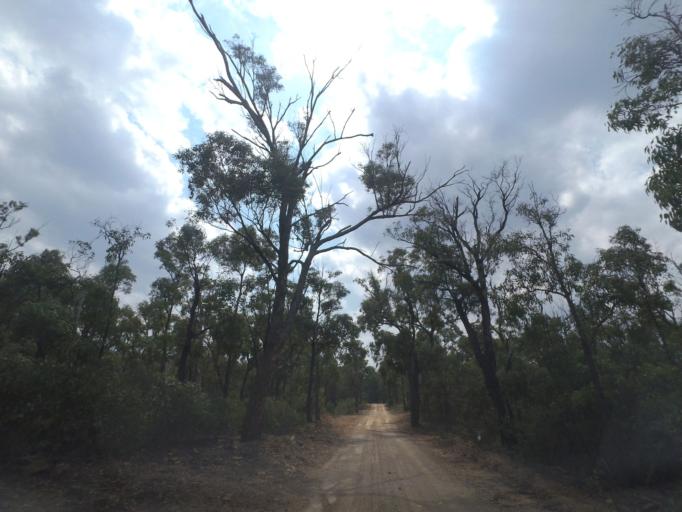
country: AU
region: Victoria
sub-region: Moorabool
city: Bacchus Marsh
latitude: -37.5673
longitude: 144.4366
